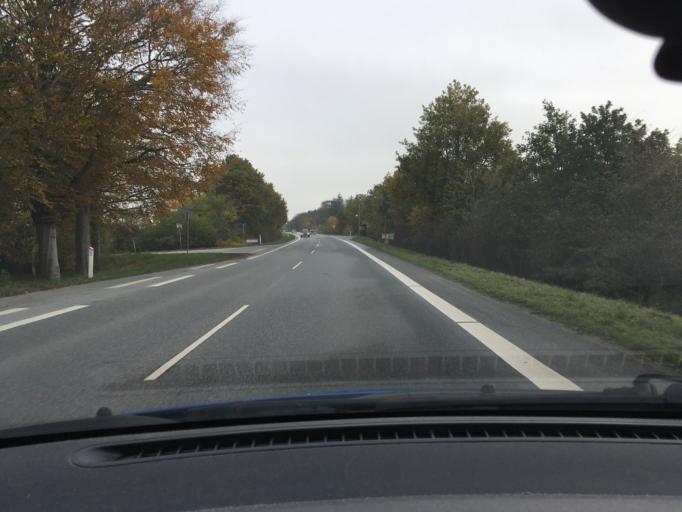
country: DK
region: South Denmark
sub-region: Aabenraa Kommune
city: Aabenraa
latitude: 54.9841
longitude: 9.3874
